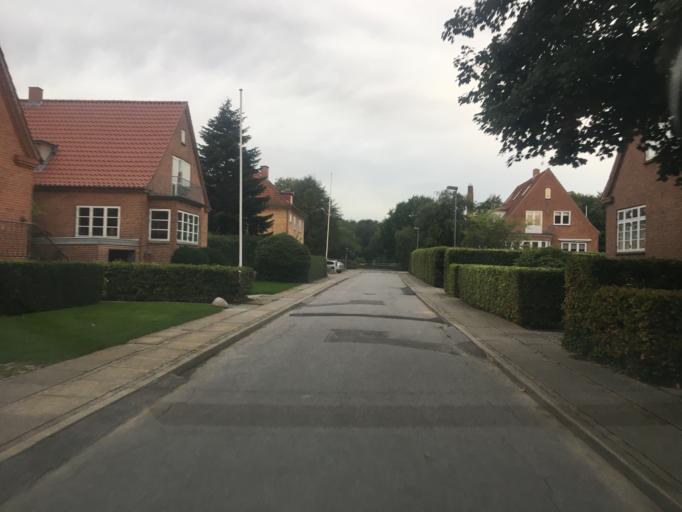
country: DK
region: South Denmark
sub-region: Tonder Kommune
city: Tonder
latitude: 54.9408
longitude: 8.8782
